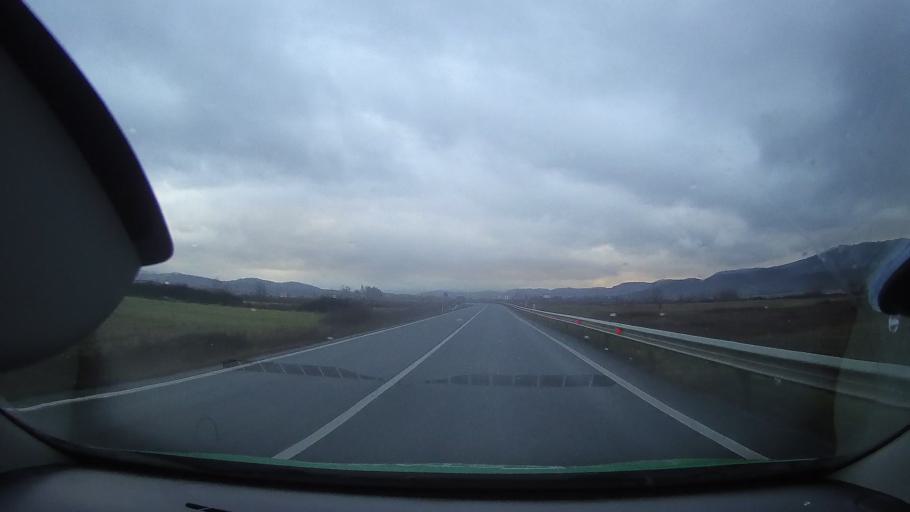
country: RO
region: Hunedoara
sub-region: Comuna Ribita
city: Ribita
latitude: 46.1679
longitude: 22.7444
